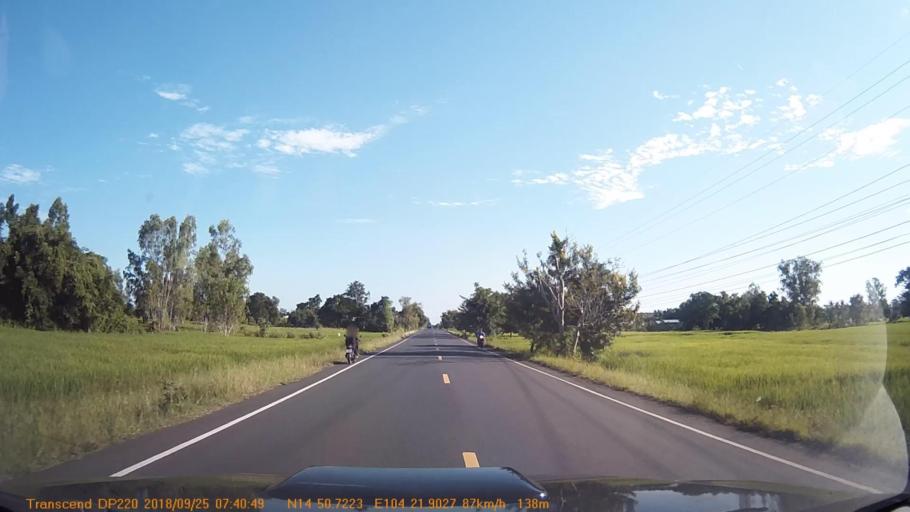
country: TH
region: Sisaket
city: Phayu
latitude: 14.8459
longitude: 104.3652
